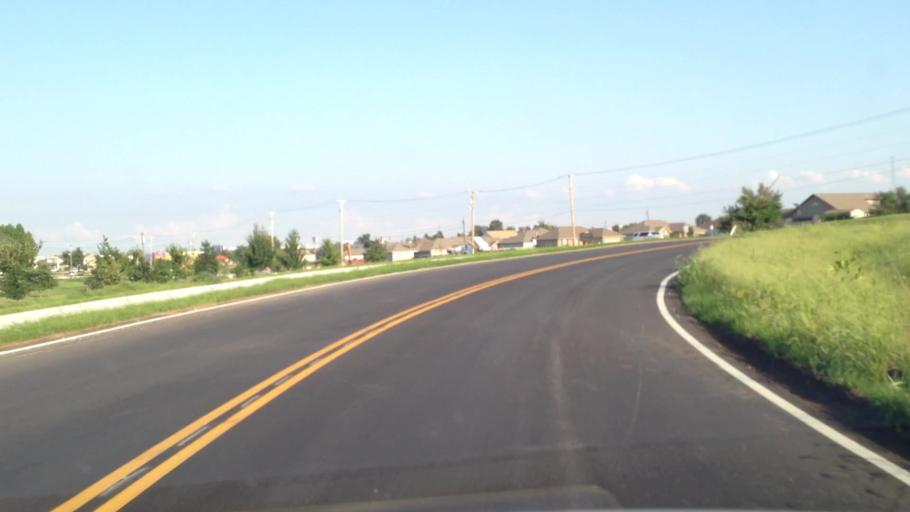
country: US
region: Missouri
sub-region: Jasper County
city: Duquesne
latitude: 37.0701
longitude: -94.4850
